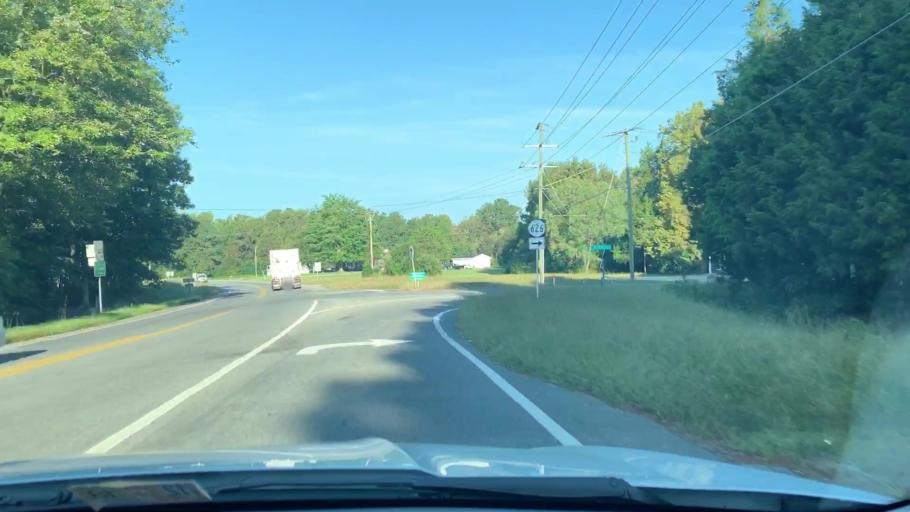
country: US
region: Virginia
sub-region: Middlesex County
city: Deltaville
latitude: 37.5543
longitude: -76.4511
